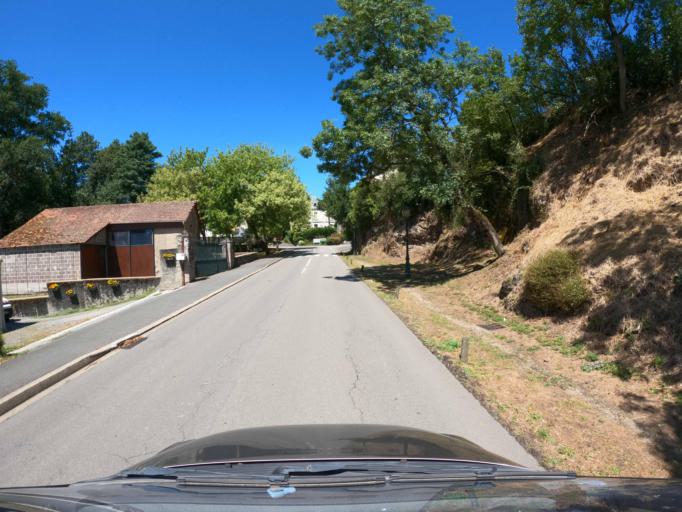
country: FR
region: Pays de la Loire
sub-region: Departement de la Loire-Atlantique
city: La Limouziniere
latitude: 46.9633
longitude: -1.5826
